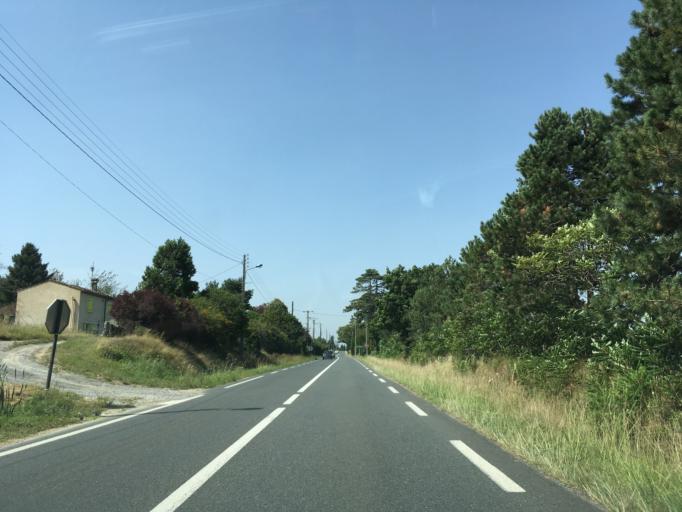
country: FR
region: Midi-Pyrenees
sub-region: Departement du Tarn
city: Burlats
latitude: 43.6210
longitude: 2.2840
